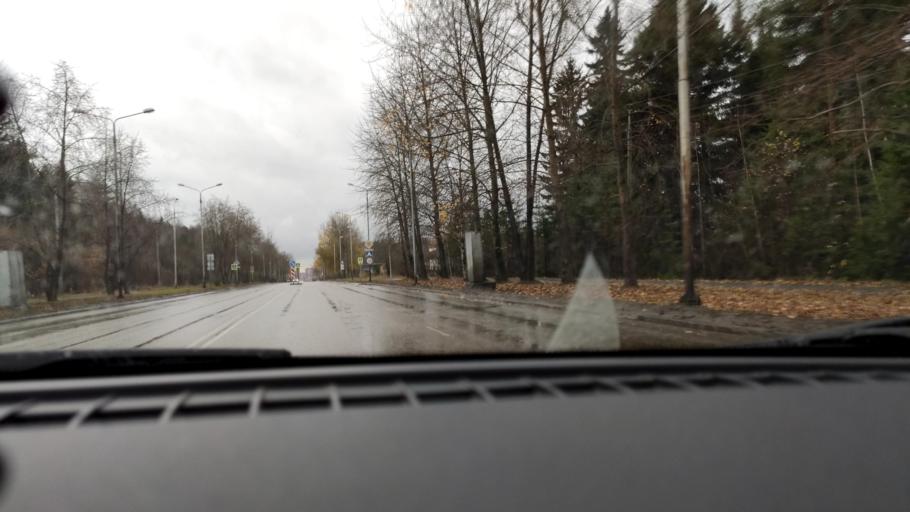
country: RU
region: Perm
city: Perm
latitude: 58.0842
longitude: 56.3768
